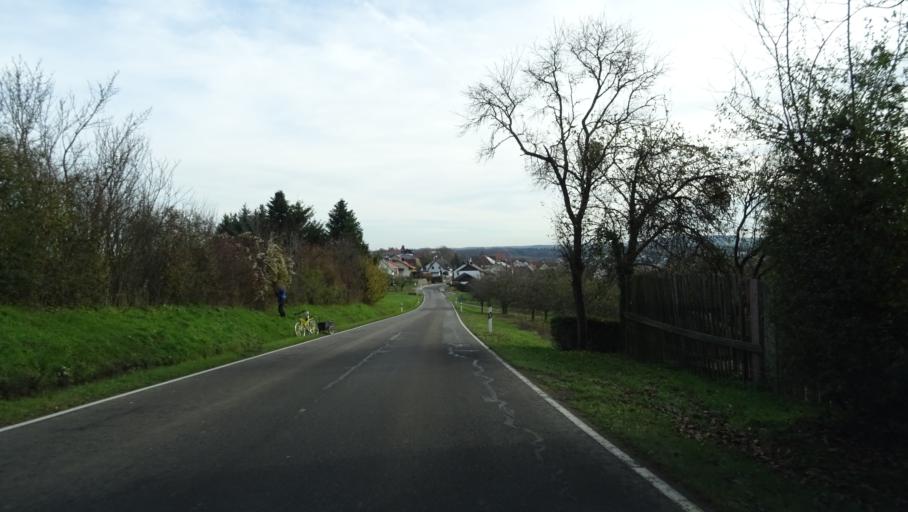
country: DE
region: Baden-Wuerttemberg
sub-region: Karlsruhe Region
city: Fahrenbach
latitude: 49.4039
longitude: 9.1283
